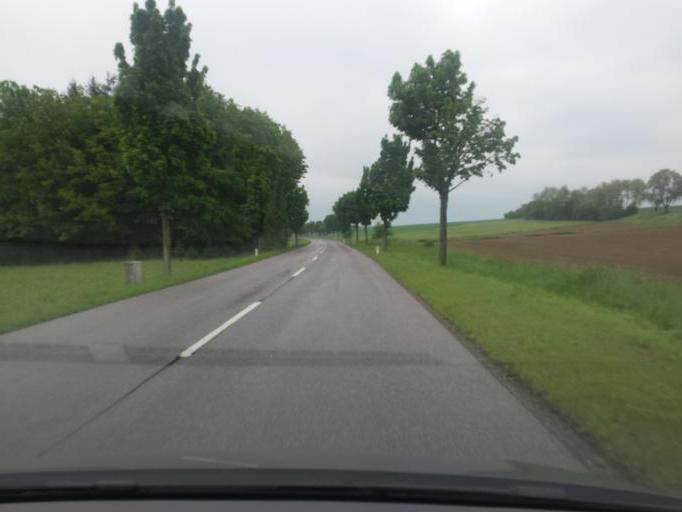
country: AT
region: Burgenland
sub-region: Politischer Bezirk Oberpullendorf
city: Lutzmannsburg
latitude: 47.4565
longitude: 16.5863
